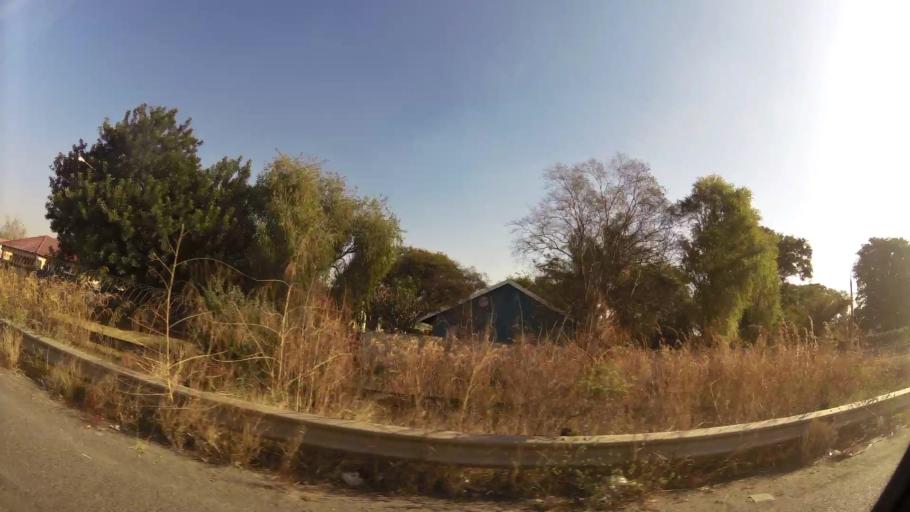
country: ZA
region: North-West
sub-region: Bojanala Platinum District Municipality
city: Rustenburg
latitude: -25.6563
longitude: 27.2636
